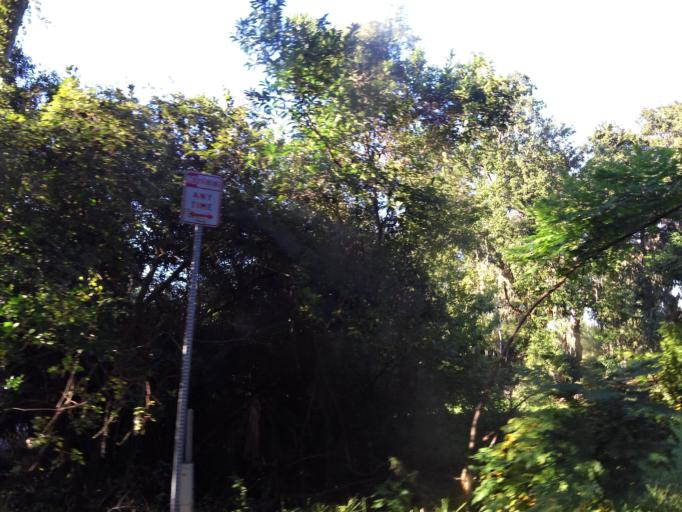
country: US
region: Florida
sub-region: Duval County
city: Jacksonville
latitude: 30.2645
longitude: -81.6443
